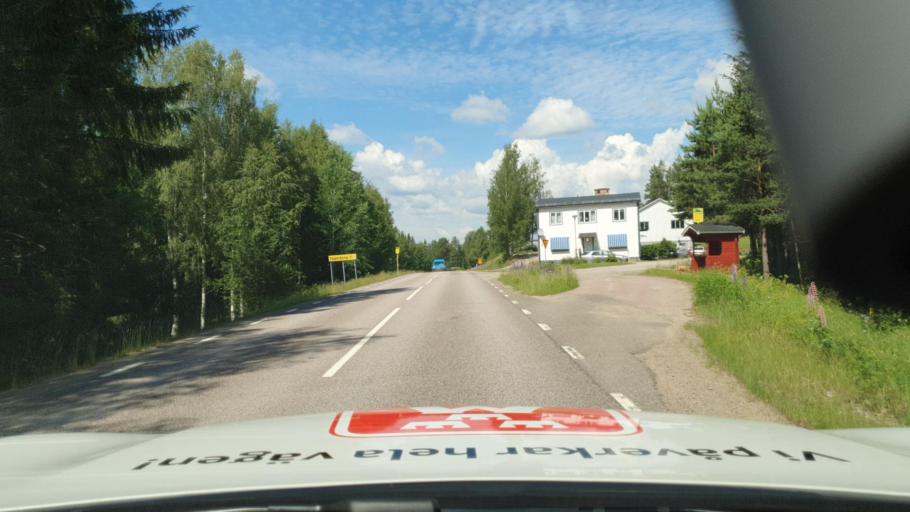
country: SE
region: Vaermland
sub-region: Torsby Kommun
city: Torsby
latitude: 60.3565
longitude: 12.9543
